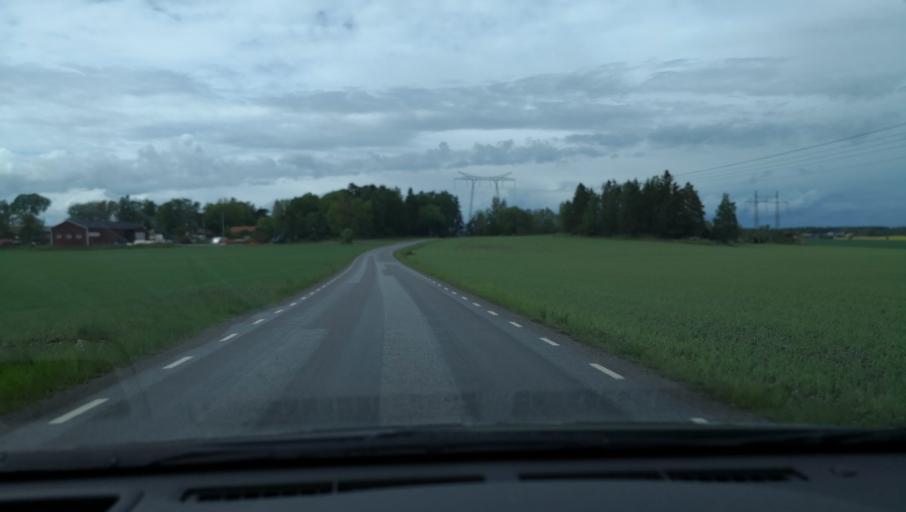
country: SE
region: Uppsala
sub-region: Enkopings Kommun
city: Orsundsbro
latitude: 59.6922
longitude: 17.3749
